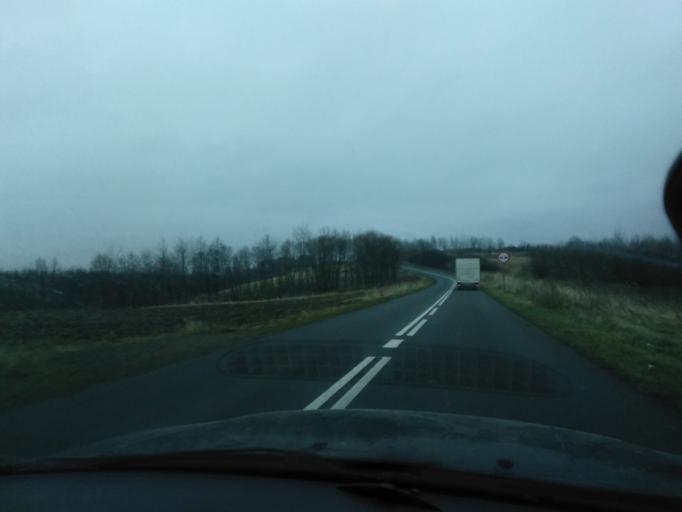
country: PL
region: Subcarpathian Voivodeship
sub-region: Powiat jaroslawski
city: Jodlowka
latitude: 49.8875
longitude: 22.4743
